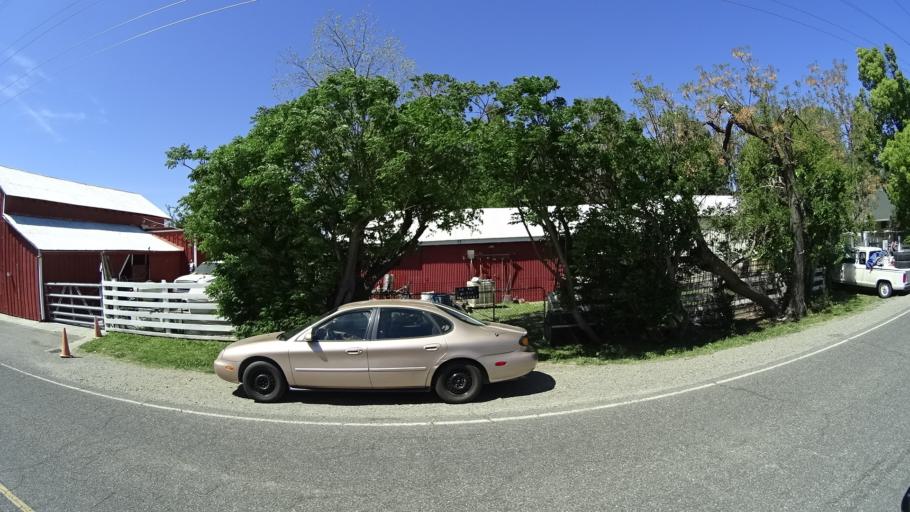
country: US
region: California
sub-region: Glenn County
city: Orland
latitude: 39.7357
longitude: -122.1781
